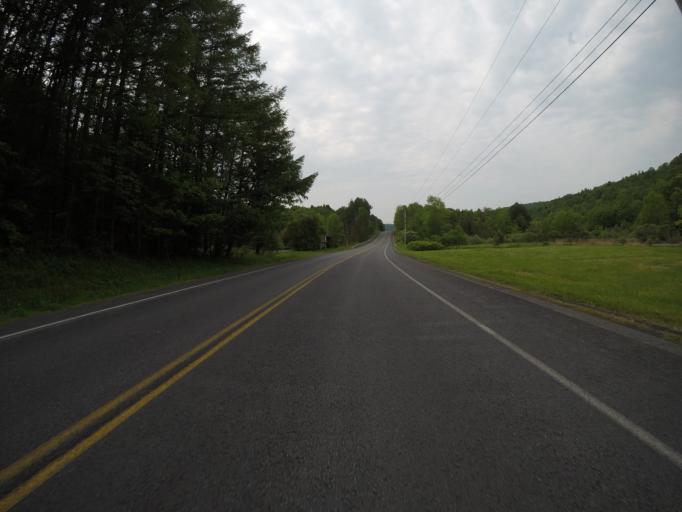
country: US
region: New York
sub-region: Sullivan County
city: Livingston Manor
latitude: 41.9955
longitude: -74.8933
